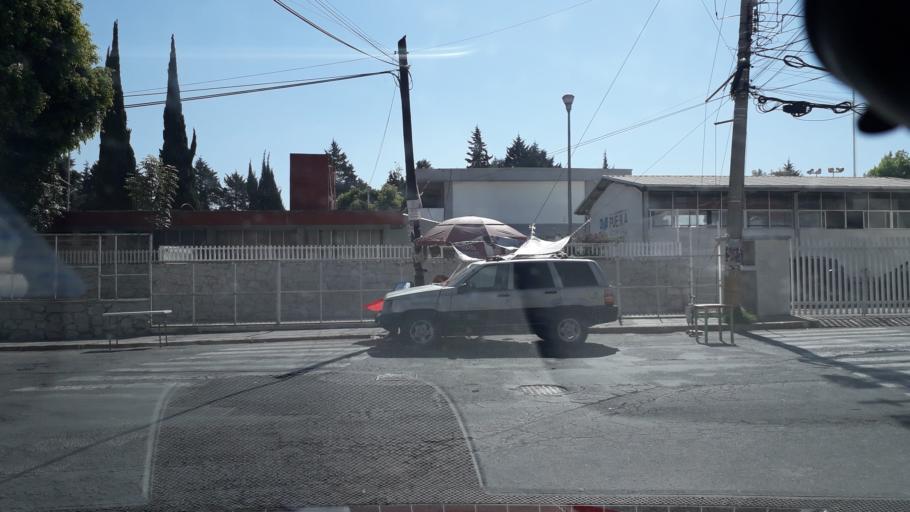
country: MX
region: Puebla
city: Puebla
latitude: 19.0763
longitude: -98.2115
